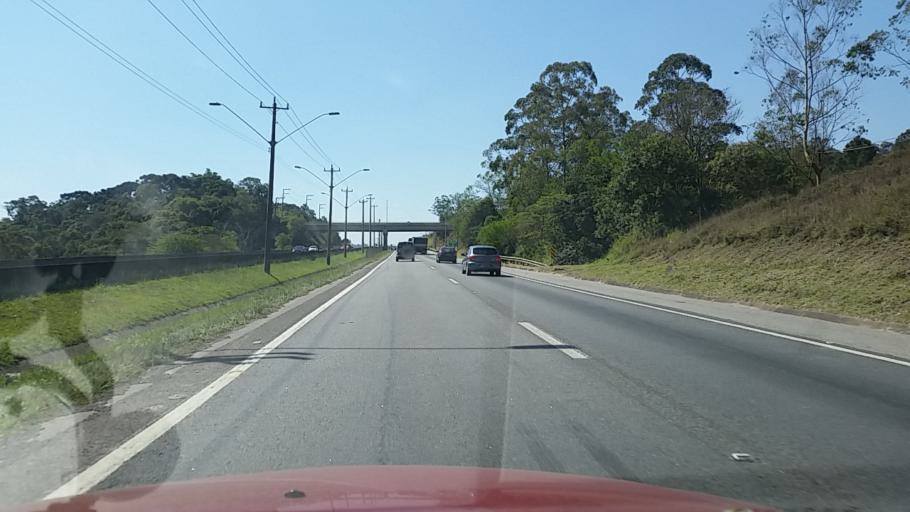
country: BR
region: Sao Paulo
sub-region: Itapecerica Da Serra
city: Itapecerica da Serra
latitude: -23.7367
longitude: -46.8962
